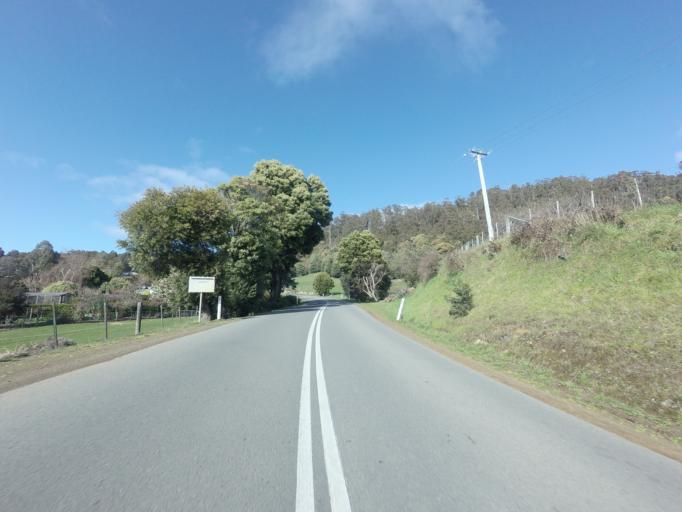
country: AU
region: Tasmania
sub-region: Huon Valley
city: Geeveston
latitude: -43.2445
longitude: 146.9911
